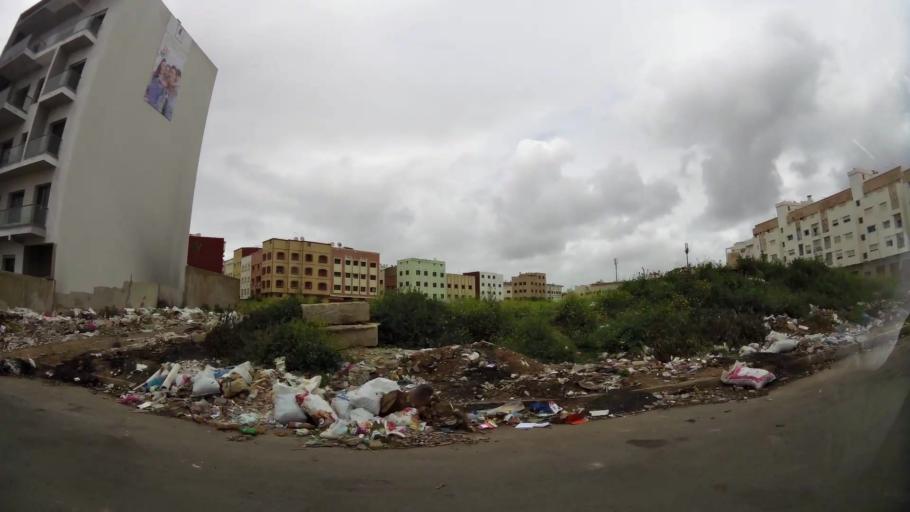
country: MA
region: Grand Casablanca
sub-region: Casablanca
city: Casablanca
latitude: 33.5288
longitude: -7.6132
